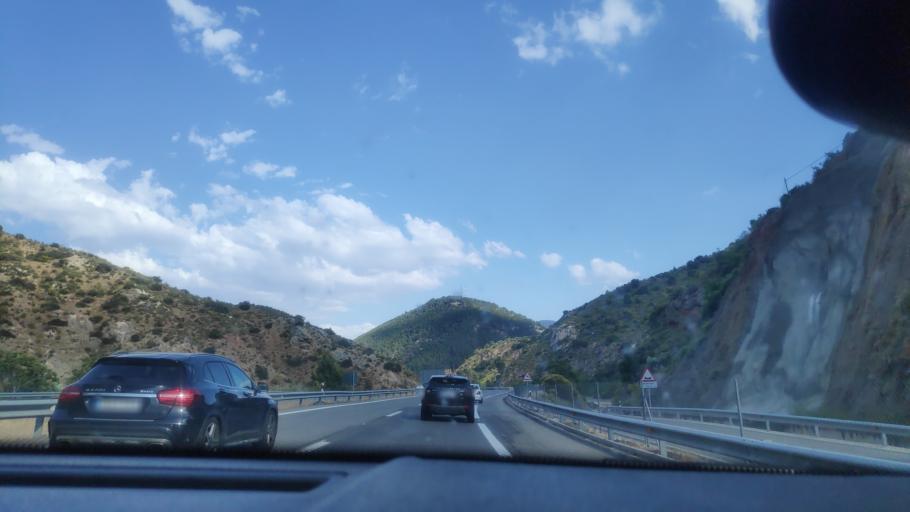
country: ES
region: Andalusia
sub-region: Provincia de Jaen
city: Cambil
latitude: 37.6622
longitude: -3.6149
